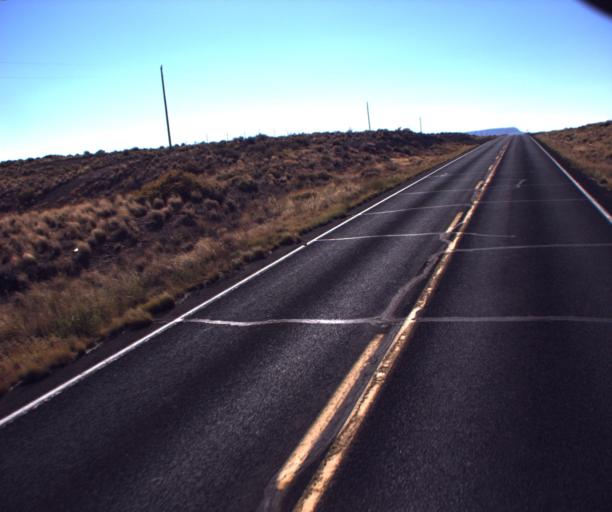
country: US
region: Arizona
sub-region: Navajo County
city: Dilkon
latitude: 35.5543
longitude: -110.4542
